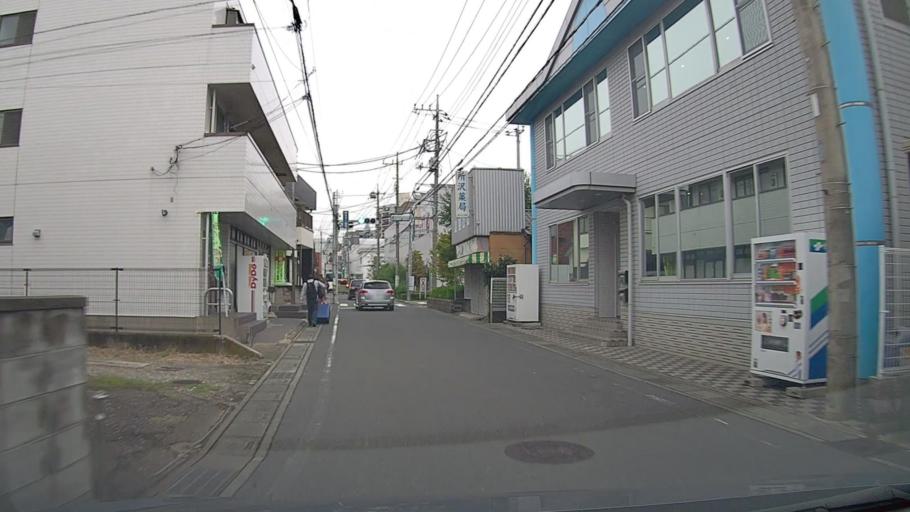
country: JP
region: Saitama
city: Tokorozawa
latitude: 35.7832
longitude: 139.4760
